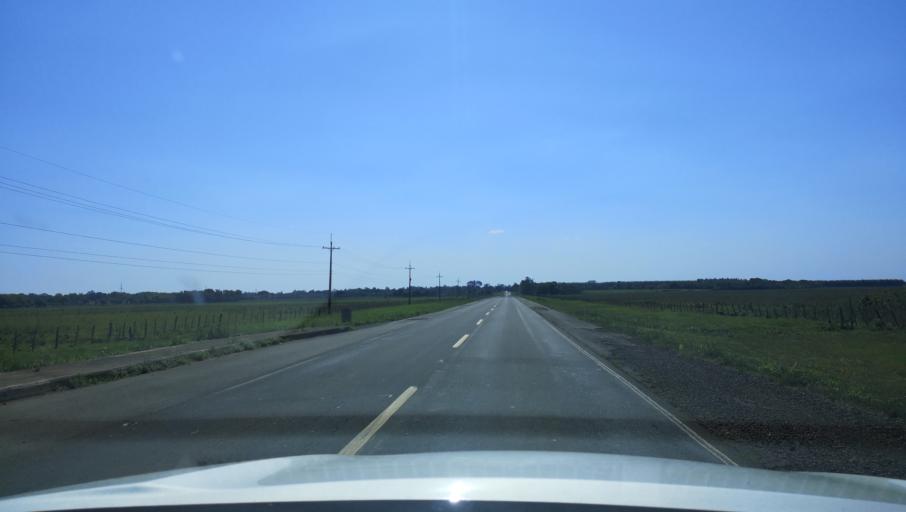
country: PY
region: Itapua
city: General Delgado
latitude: -27.0810
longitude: -56.5634
